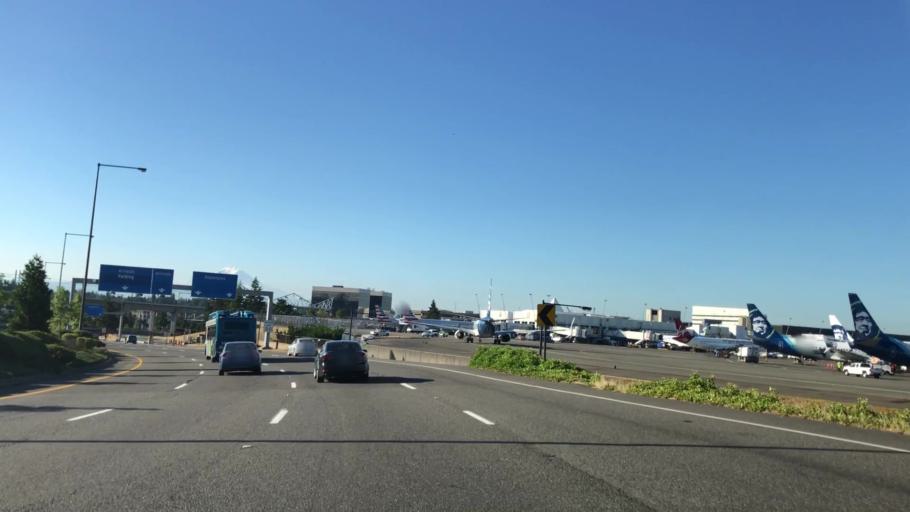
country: US
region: Washington
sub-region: King County
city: SeaTac
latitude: 47.4497
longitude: -122.3004
